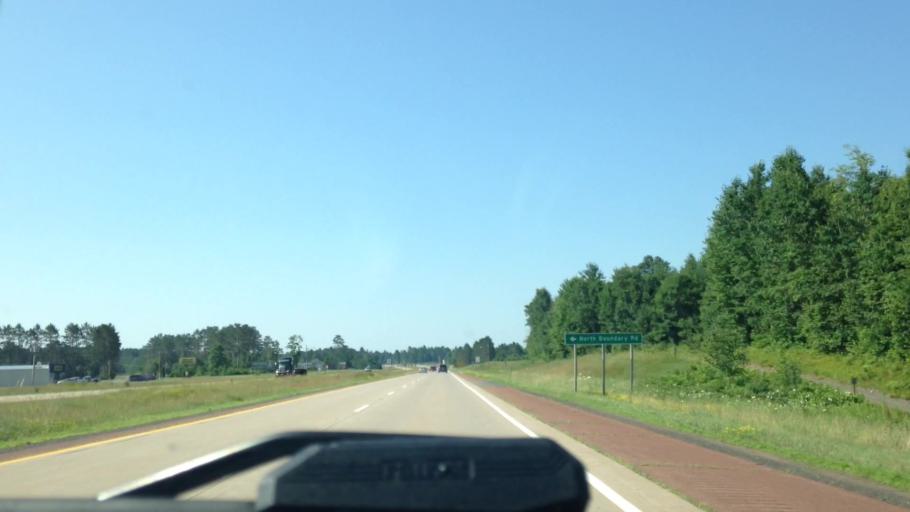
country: US
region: Wisconsin
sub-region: Douglas County
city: Lake Nebagamon
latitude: 46.3626
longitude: -91.8319
